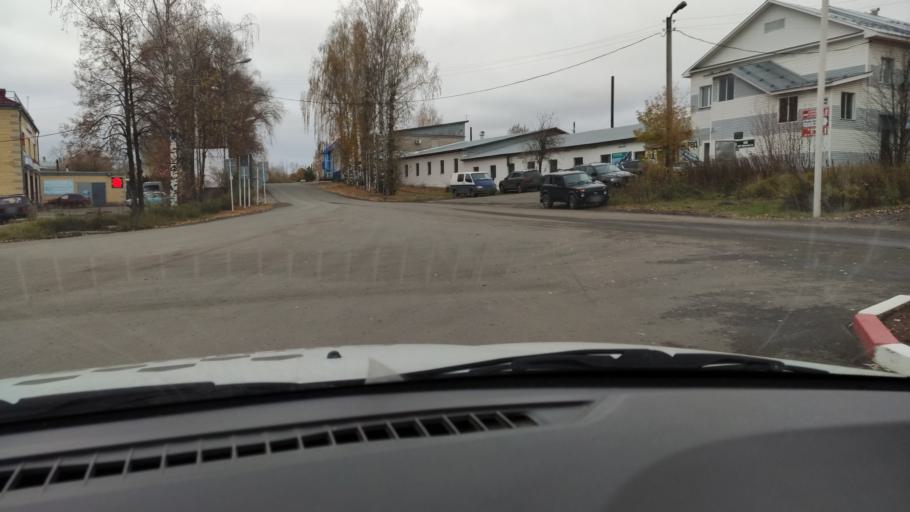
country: RU
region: Kirov
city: Slobodskoy
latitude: 58.7189
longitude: 50.1757
